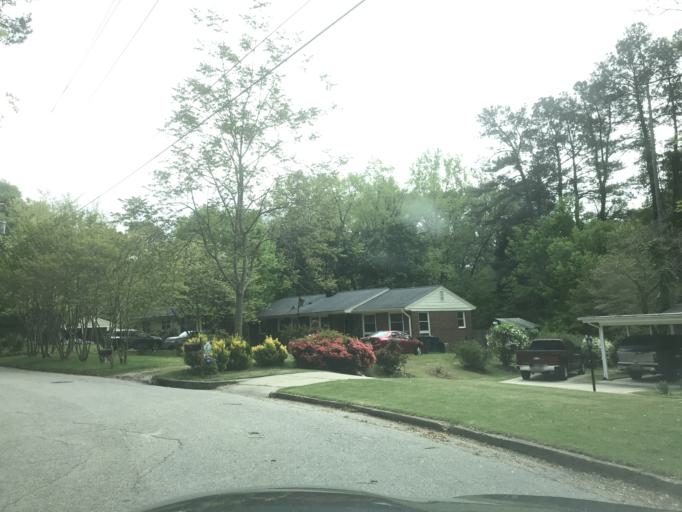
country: US
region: North Carolina
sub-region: Wake County
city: West Raleigh
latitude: 35.7765
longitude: -78.7133
